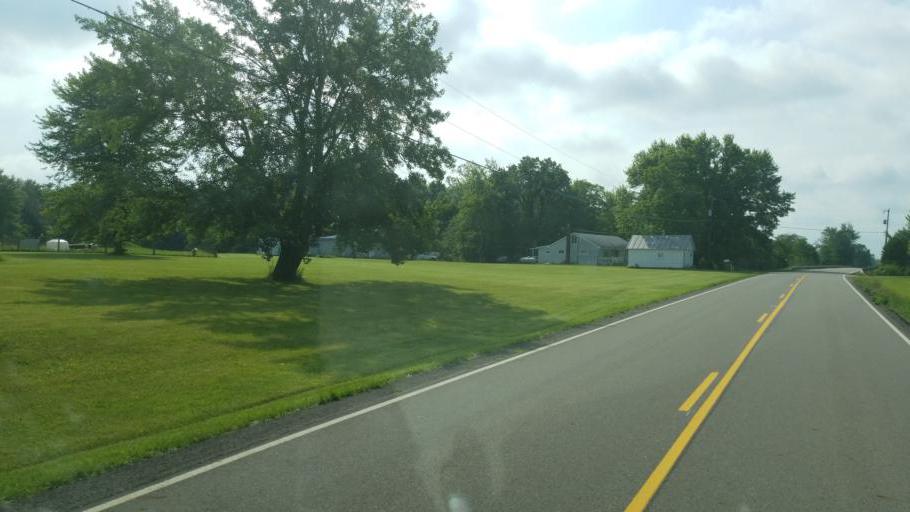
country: US
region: Ohio
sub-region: Knox County
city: Centerburg
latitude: 40.2946
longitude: -82.6350
